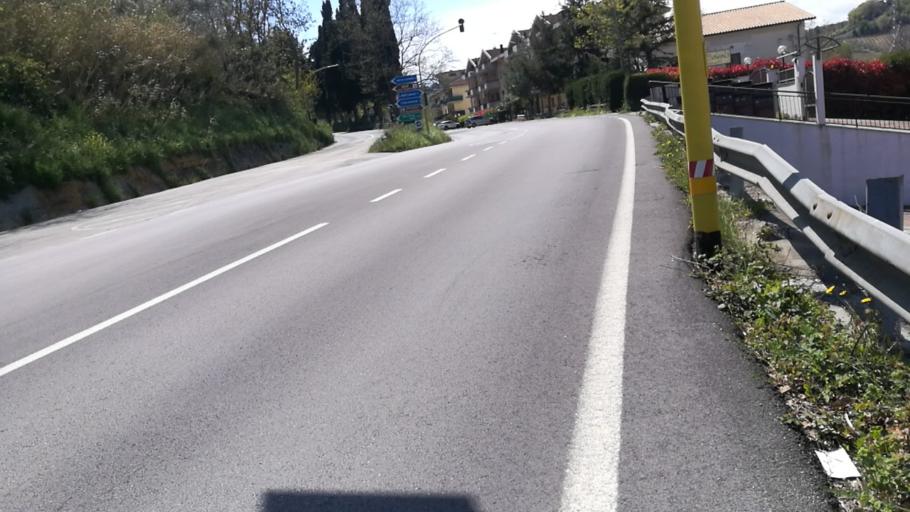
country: IT
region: Abruzzo
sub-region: Provincia di Chieti
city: Marina di San Vito
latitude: 42.3048
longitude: 14.4424
